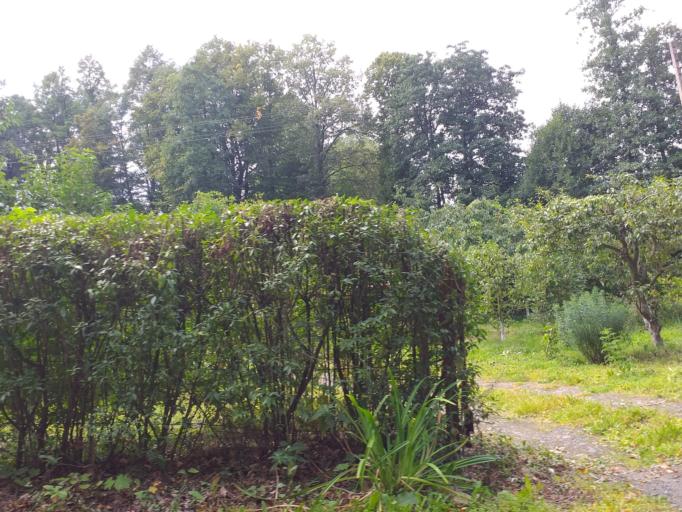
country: PL
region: Lower Silesian Voivodeship
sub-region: Powiat lubanski
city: Lesna
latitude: 51.0124
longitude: 15.3096
